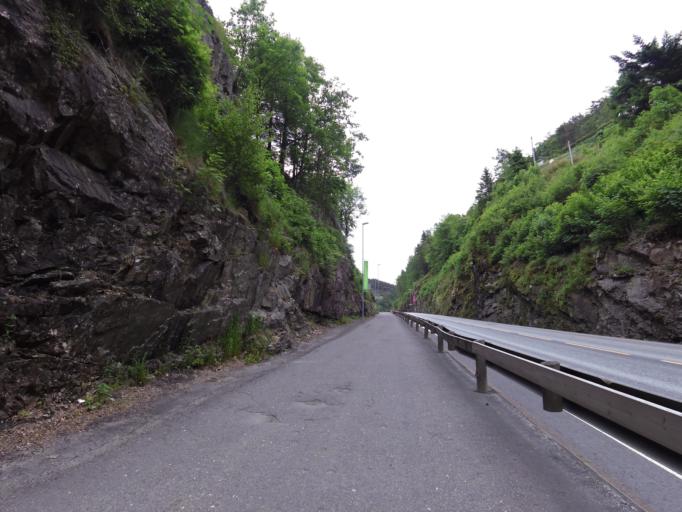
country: NO
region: Vest-Agder
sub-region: Flekkefjord
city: Flekkefjord
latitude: 58.2967
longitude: 6.6713
